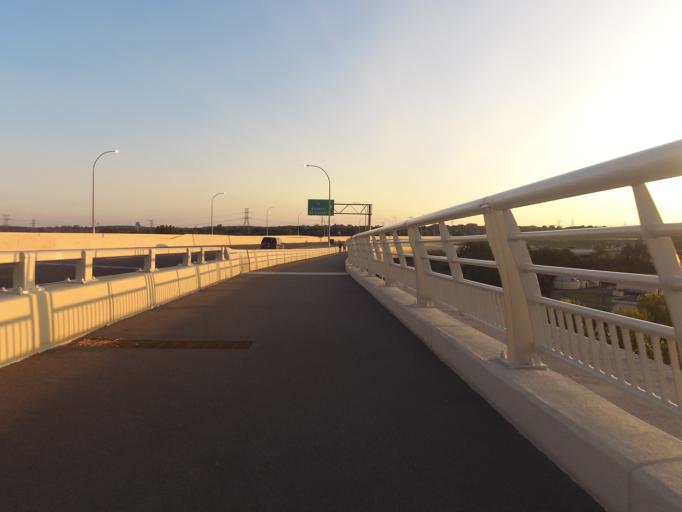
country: US
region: Minnesota
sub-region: Washington County
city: Oak Park Heights
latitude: 45.0390
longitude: -92.7878
